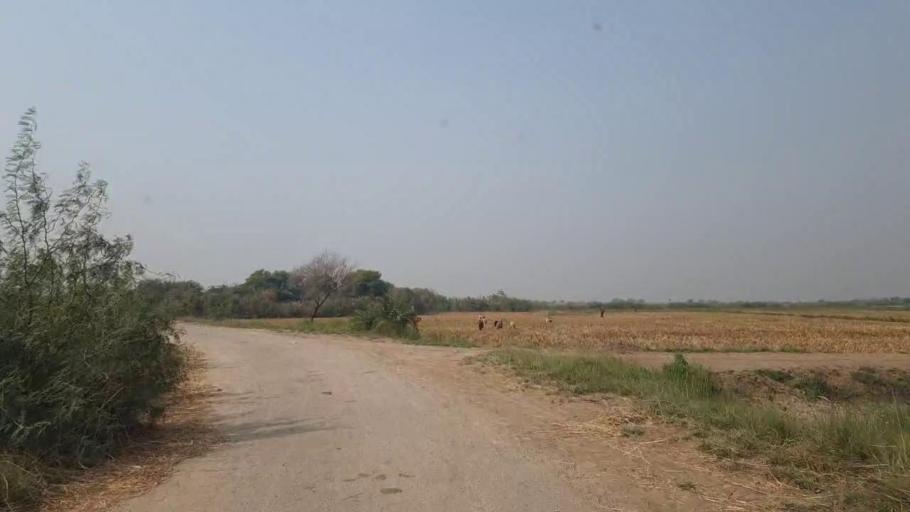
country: PK
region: Sindh
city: Matli
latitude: 25.1234
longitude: 68.6544
